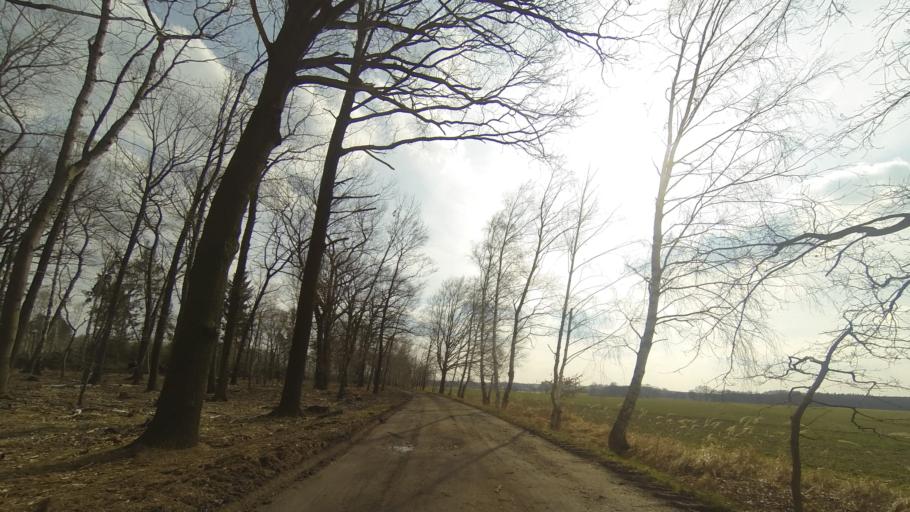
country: DE
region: Saxony
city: Radeburg
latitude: 51.2498
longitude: 13.7036
